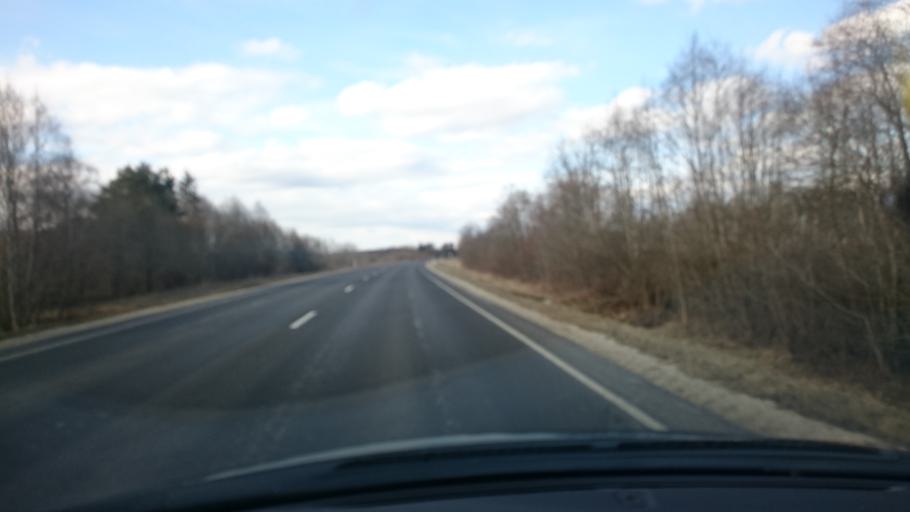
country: EE
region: Laeaene
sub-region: Lihula vald
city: Lihula
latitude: 58.8310
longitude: 24.0547
